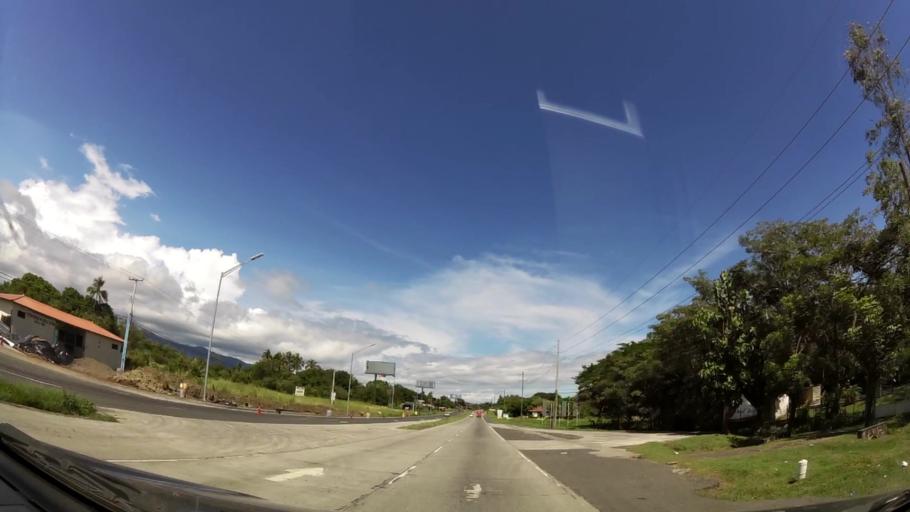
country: PA
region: Panama
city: Chame
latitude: 8.5531
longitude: -79.9074
